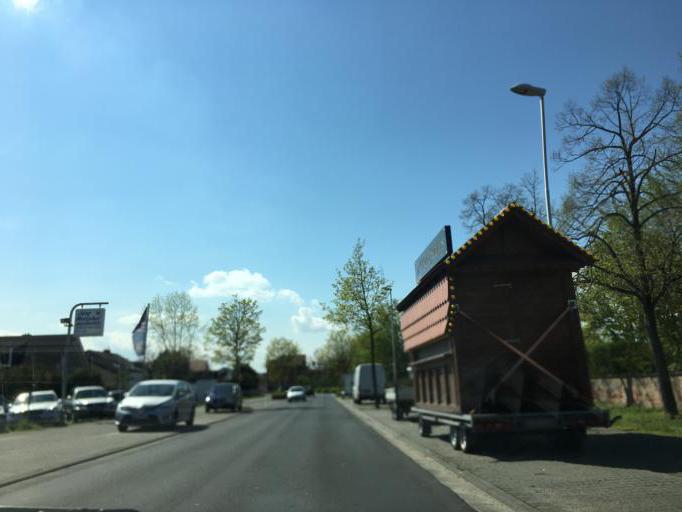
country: DE
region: Hesse
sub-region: Regierungsbezirk Darmstadt
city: Rodgau
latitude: 50.0131
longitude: 8.8904
